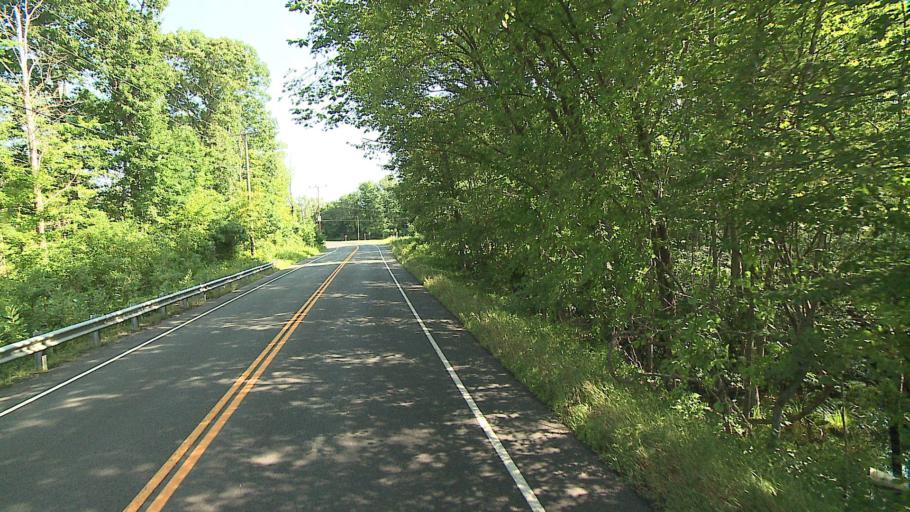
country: US
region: Connecticut
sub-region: Fairfield County
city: Georgetown
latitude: 41.2908
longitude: -73.4509
